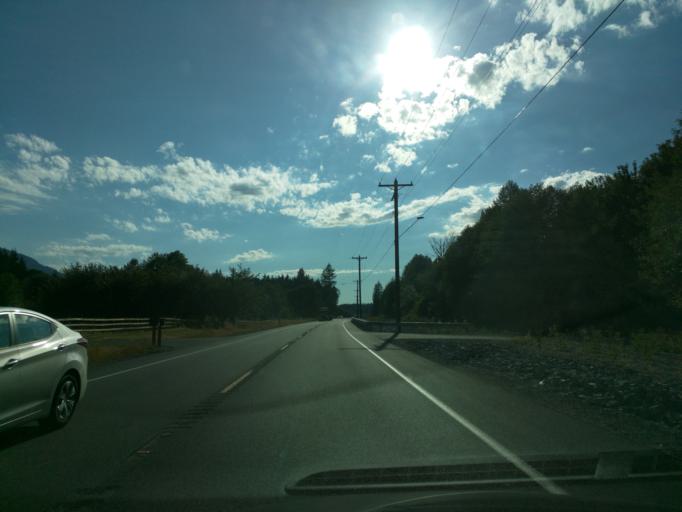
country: US
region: Washington
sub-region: Snohomish County
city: Darrington
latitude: 48.2772
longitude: -121.8255
